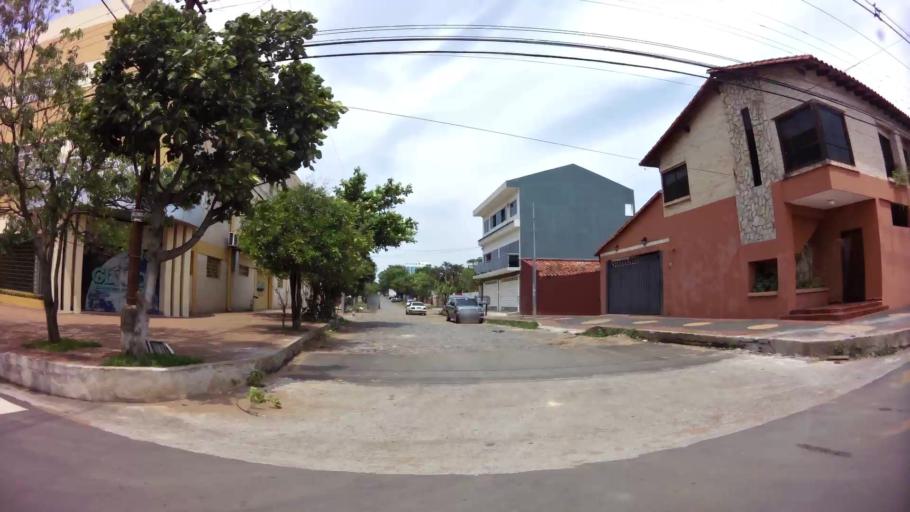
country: PY
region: Central
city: Fernando de la Mora
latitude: -25.3152
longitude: -57.5614
